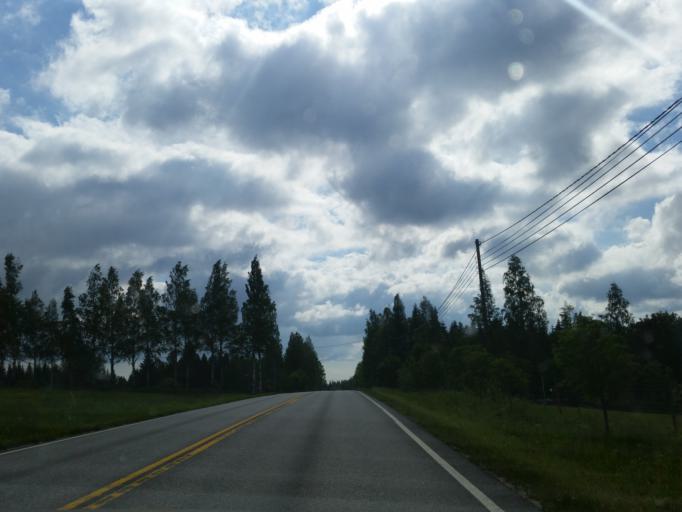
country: FI
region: Northern Savo
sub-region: Kuopio
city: Kuopio
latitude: 62.8467
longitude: 27.3975
